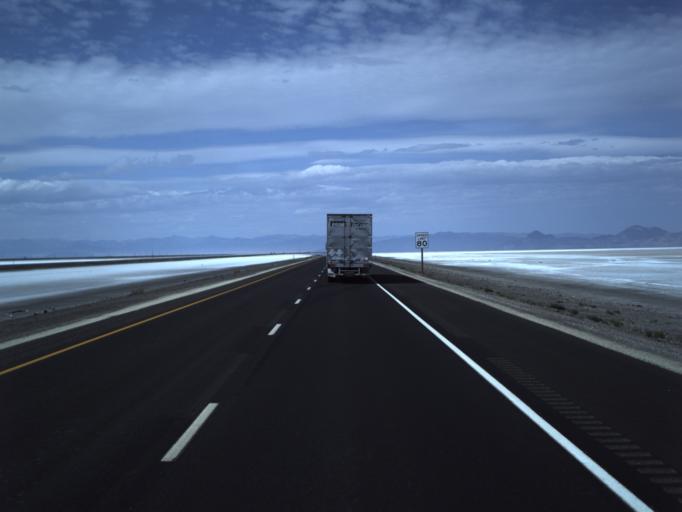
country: US
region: Utah
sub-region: Tooele County
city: Wendover
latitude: 40.7353
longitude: -113.6556
